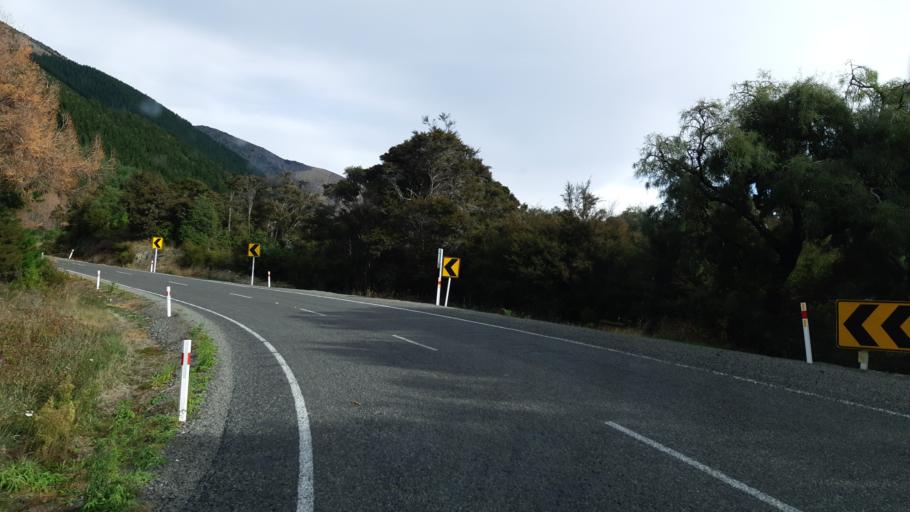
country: NZ
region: Tasman
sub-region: Tasman District
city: Wakefield
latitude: -41.7100
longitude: 173.1152
